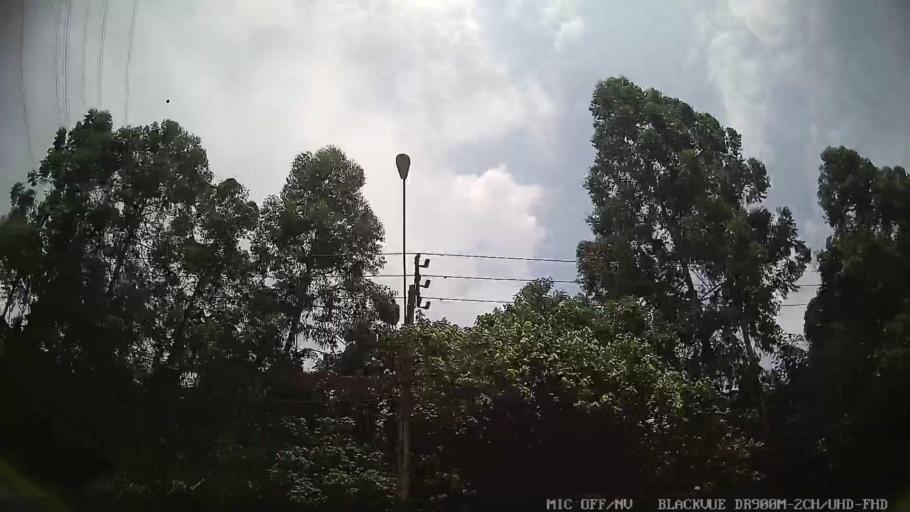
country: BR
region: Sao Paulo
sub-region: Osasco
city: Osasco
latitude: -23.4908
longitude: -46.7671
